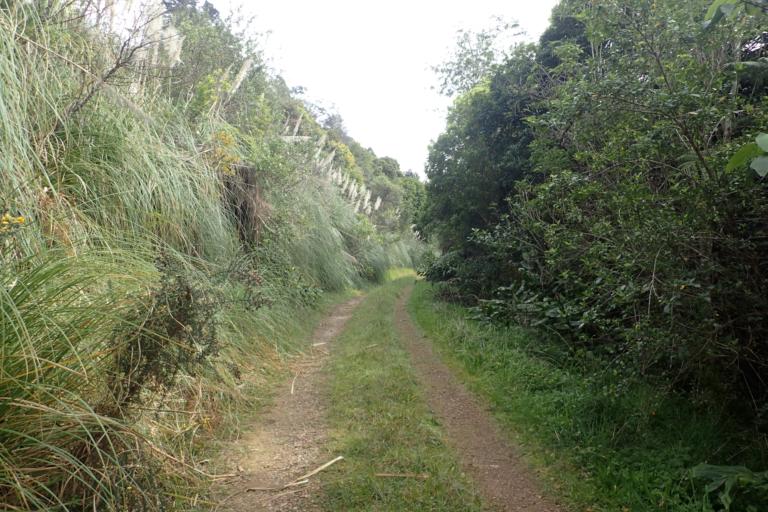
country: NZ
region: Auckland
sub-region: Auckland
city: Pakuranga
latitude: -36.7869
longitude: 175.0054
